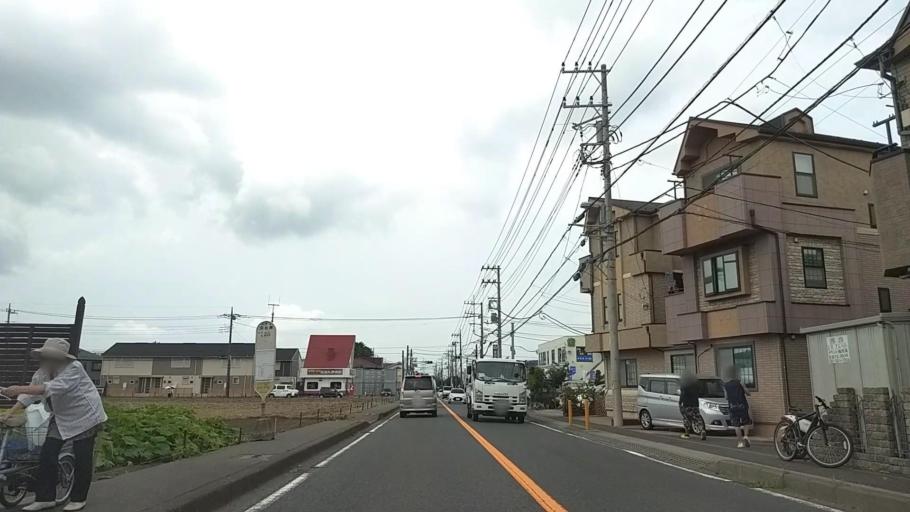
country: JP
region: Kanagawa
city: Minami-rinkan
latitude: 35.4350
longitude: 139.4419
